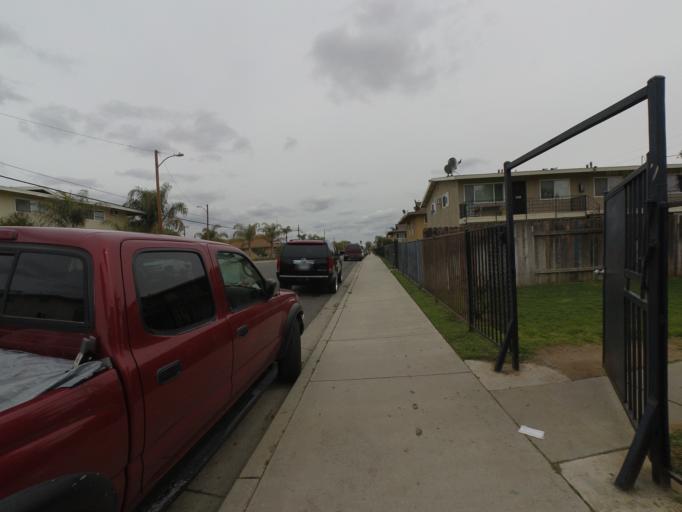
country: US
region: California
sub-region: Riverside County
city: March Air Force Base
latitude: 33.9183
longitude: -117.2695
